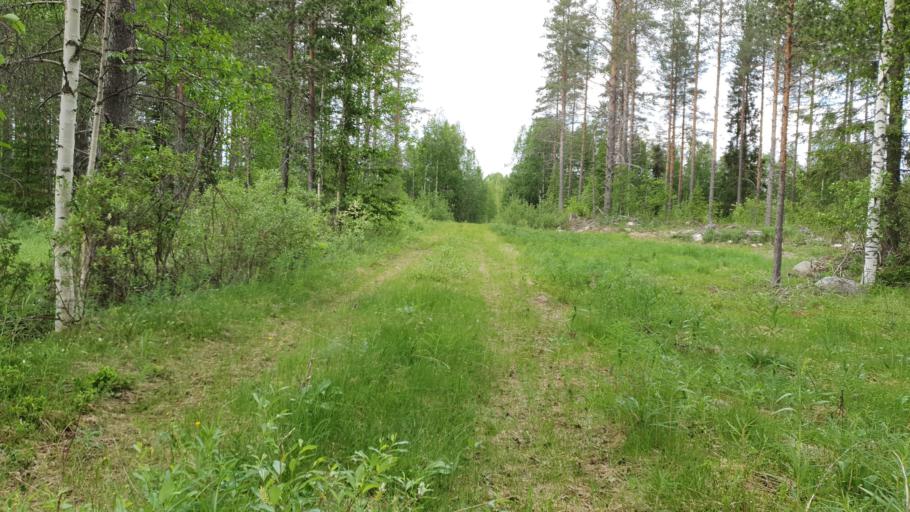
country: FI
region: Kainuu
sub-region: Kehys-Kainuu
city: Kuhmo
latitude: 64.4494
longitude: 29.6663
